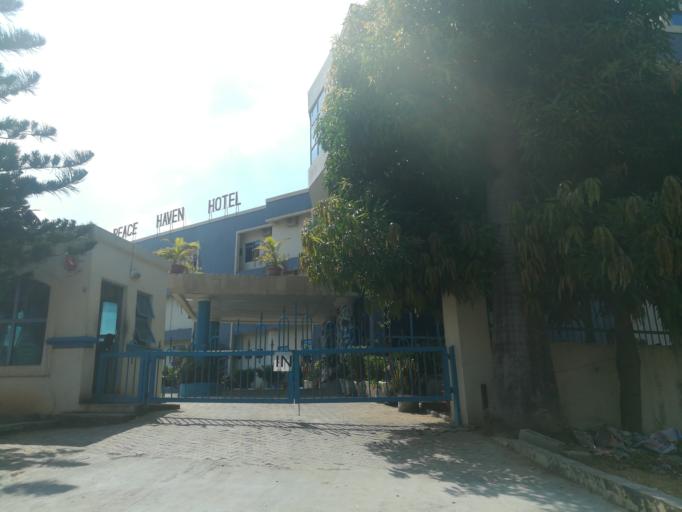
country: NG
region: Abuja Federal Capital Territory
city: Abuja
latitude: 9.0536
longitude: 7.4488
